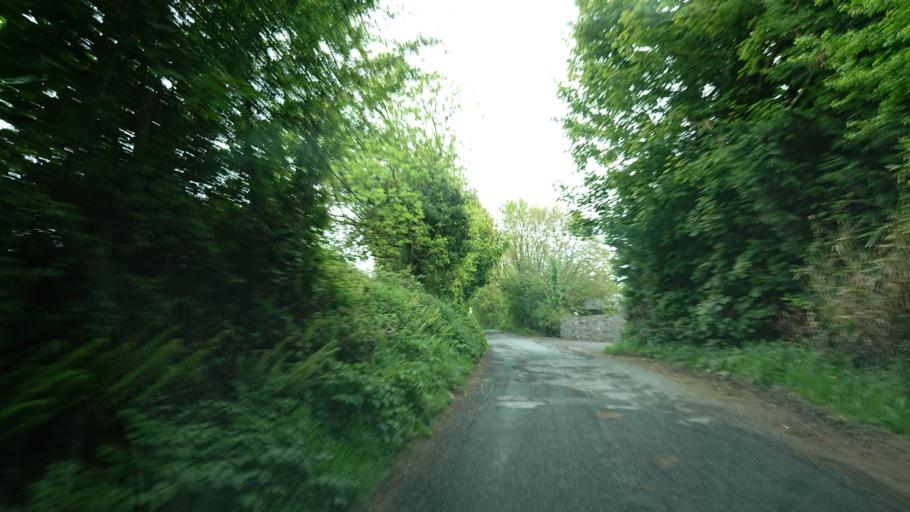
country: IE
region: Munster
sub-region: Waterford
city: Dunmore East
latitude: 52.2267
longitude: -7.0288
